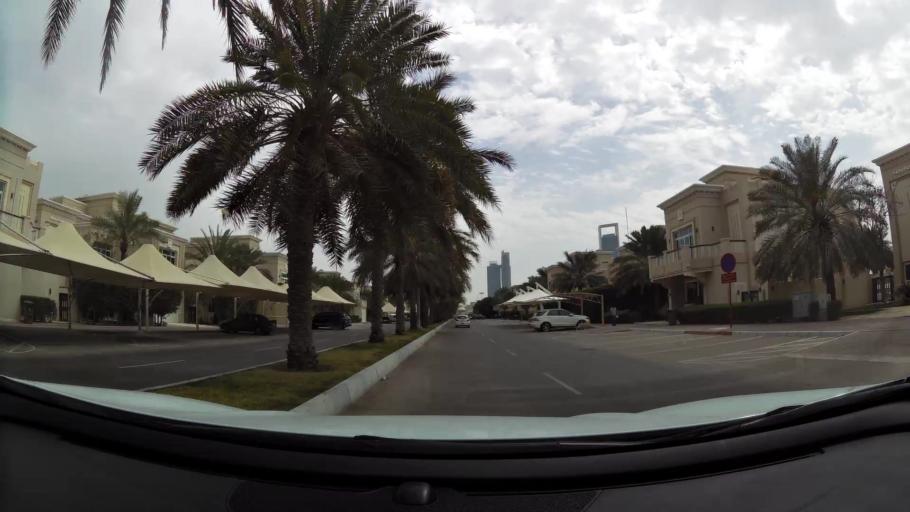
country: AE
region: Abu Dhabi
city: Abu Dhabi
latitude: 24.4753
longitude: 54.3148
